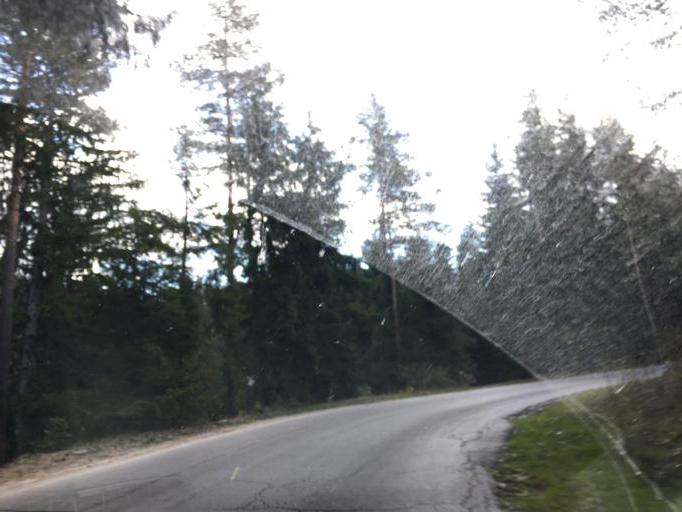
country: BG
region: Pazardzhik
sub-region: Obshtina Batak
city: Batak
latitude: 41.9257
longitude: 24.2825
